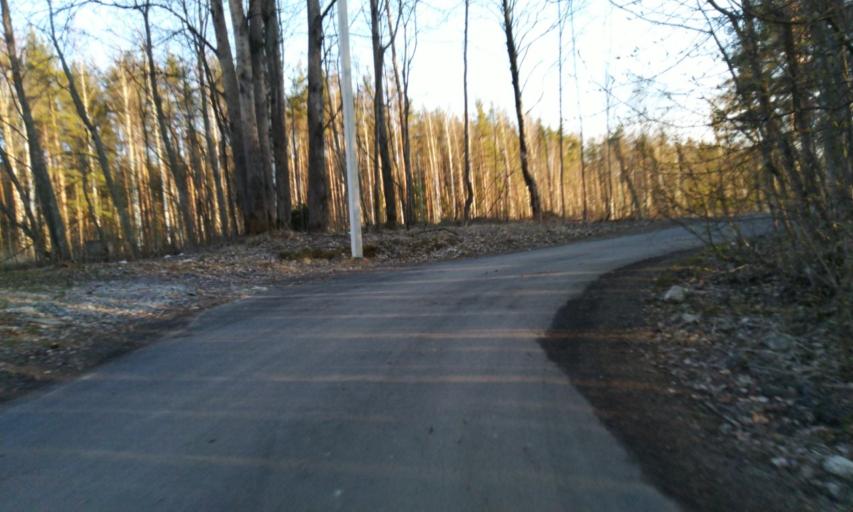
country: RU
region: Leningrad
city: Novoye Devyatkino
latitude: 60.1099
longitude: 30.4619
